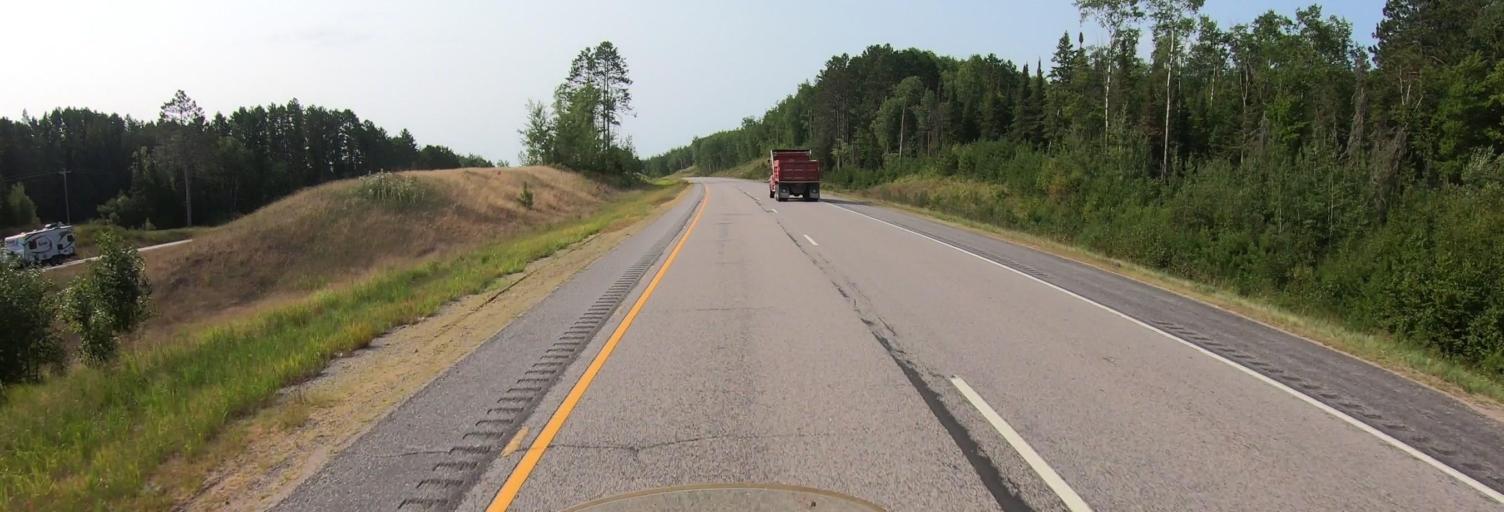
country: US
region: Minnesota
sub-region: Saint Louis County
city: Mountain Iron
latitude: 47.6836
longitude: -92.6532
